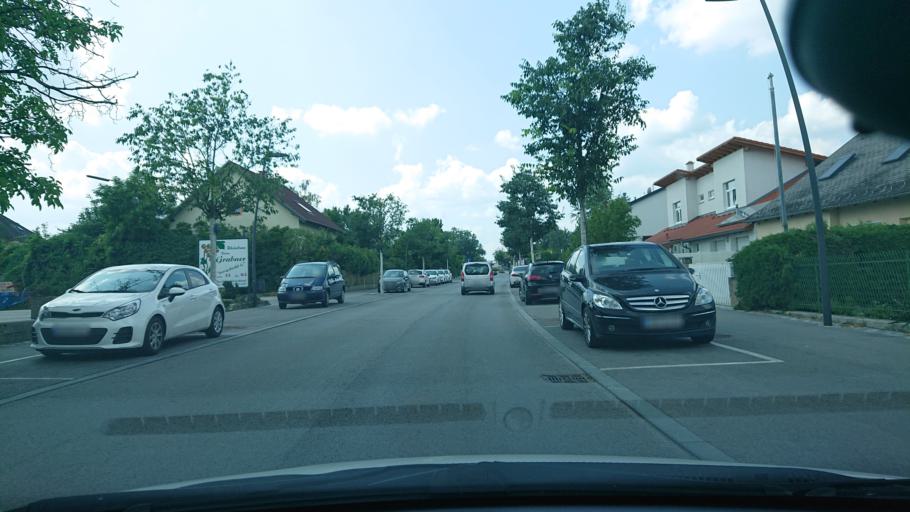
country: AT
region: Lower Austria
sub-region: Politischer Bezirk Baden
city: Kottingbrunn
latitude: 47.9487
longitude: 16.2244
